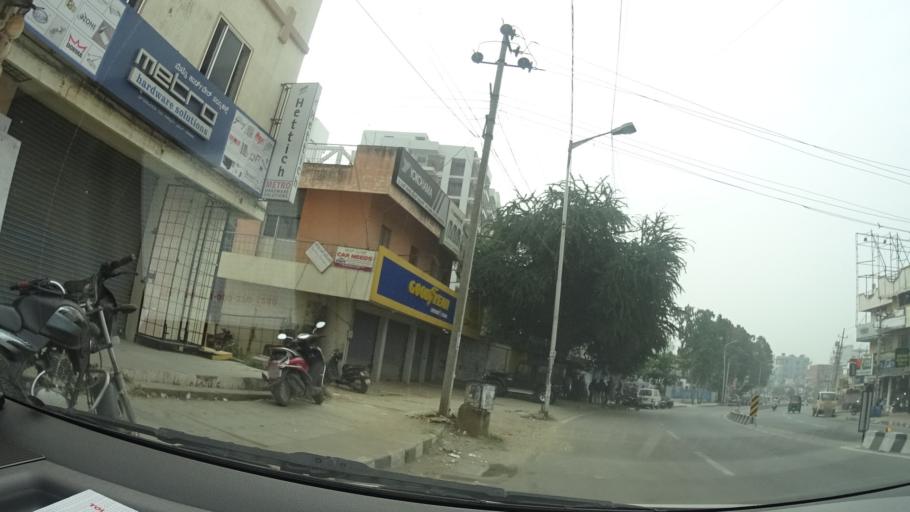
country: IN
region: Karnataka
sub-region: Bangalore Urban
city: Bangalore
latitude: 13.0247
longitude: 77.6305
